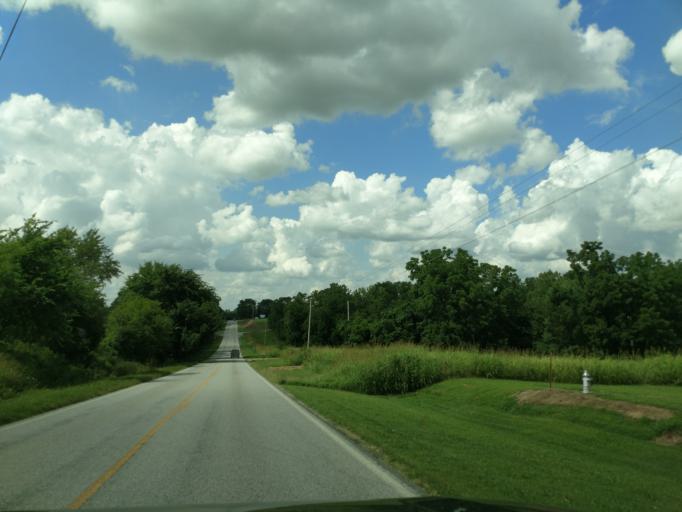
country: US
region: Arkansas
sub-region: Carroll County
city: Berryville
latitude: 36.3989
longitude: -93.5660
